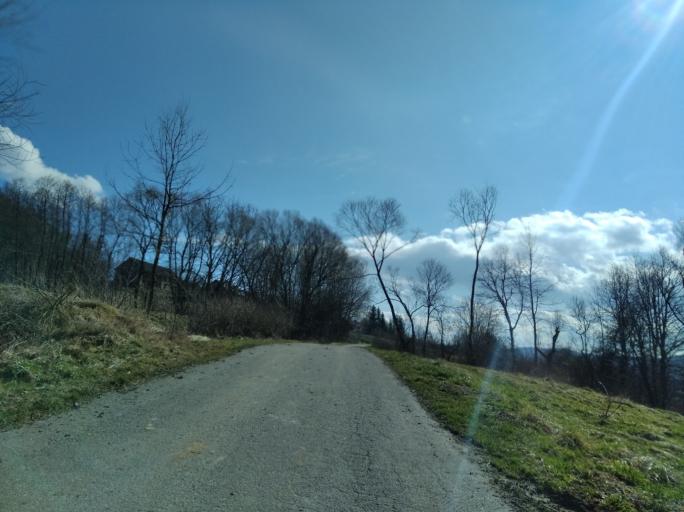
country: PL
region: Subcarpathian Voivodeship
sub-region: Powiat strzyzowski
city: Wysoka Strzyzowska
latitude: 49.8065
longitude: 21.7519
